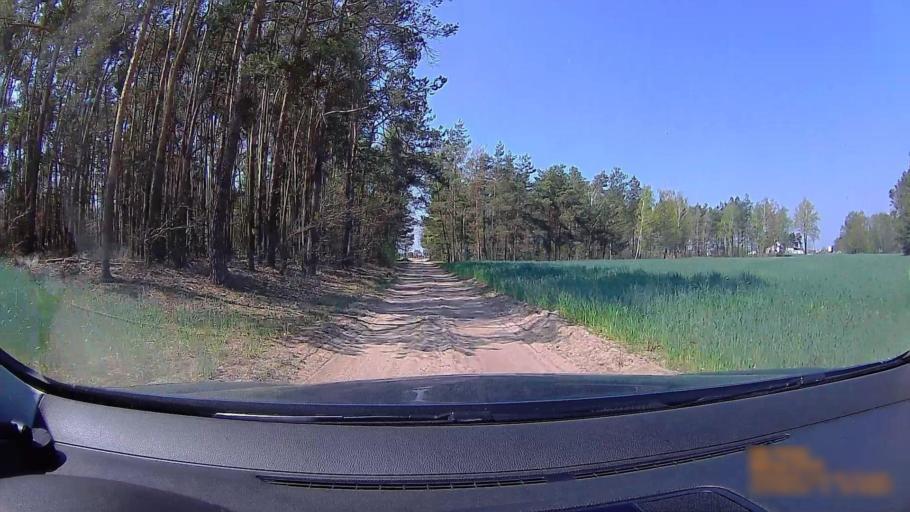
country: PL
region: Greater Poland Voivodeship
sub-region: Powiat koninski
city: Rychwal
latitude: 52.1024
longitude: 18.1742
